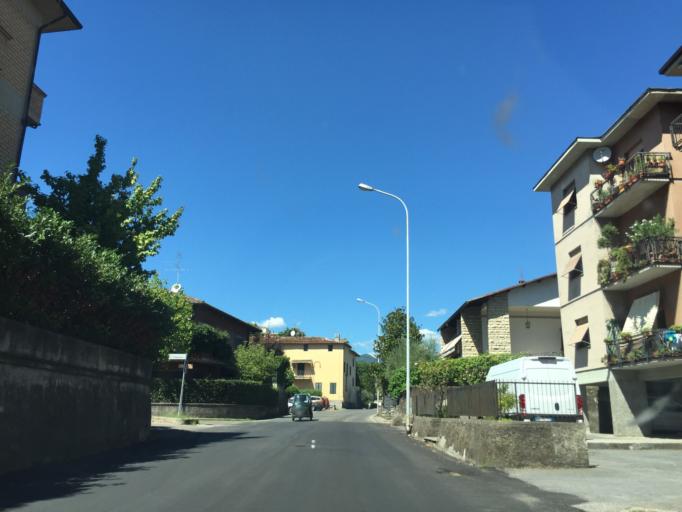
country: IT
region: Tuscany
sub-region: Provincia di Pistoia
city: Pistoia
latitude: 43.9468
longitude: 10.9105
